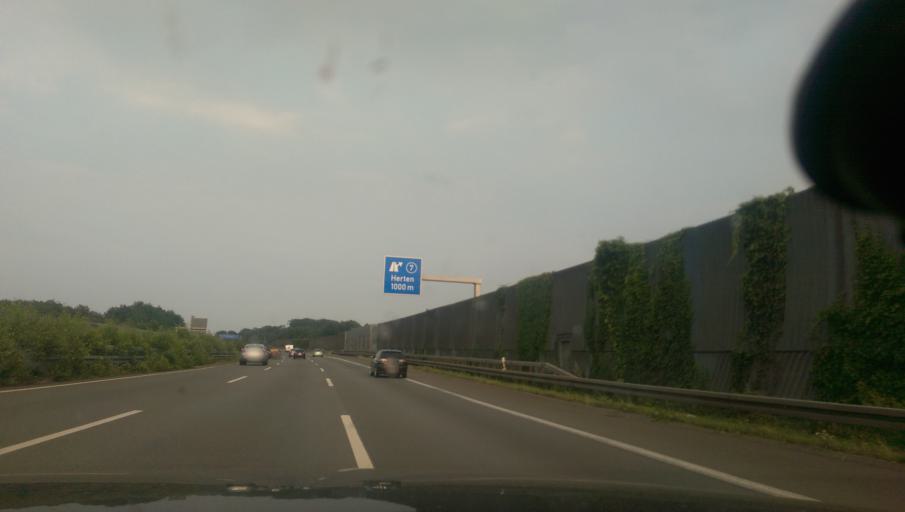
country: DE
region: North Rhine-Westphalia
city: Herten
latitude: 51.5700
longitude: 7.1119
